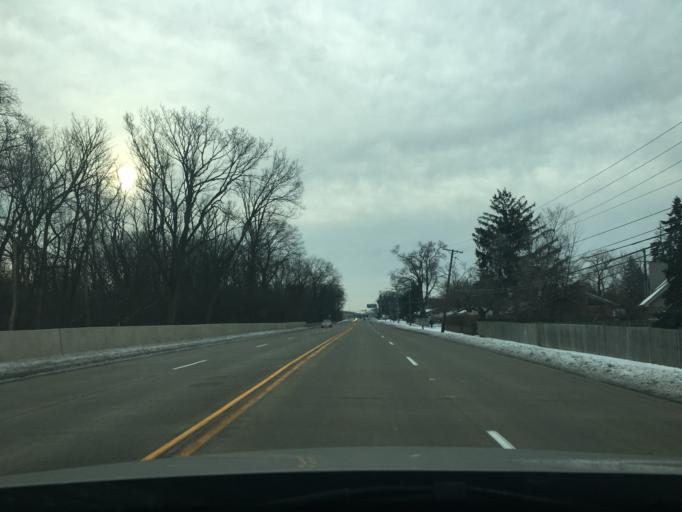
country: US
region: Illinois
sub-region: Cook County
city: Des Plaines
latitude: 42.0160
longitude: -87.8734
